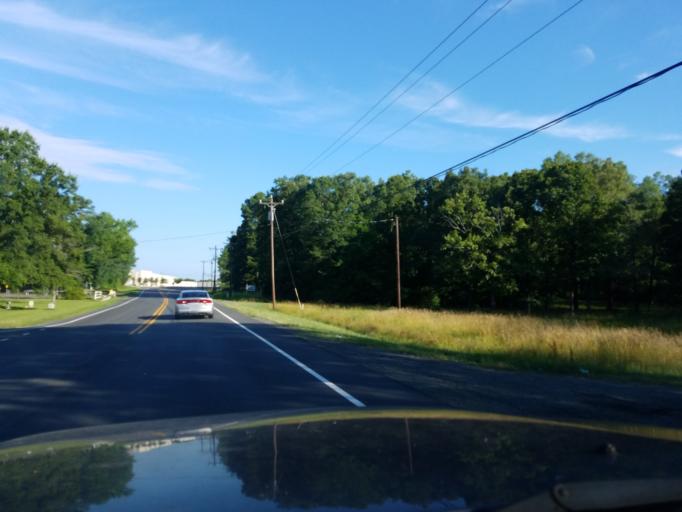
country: US
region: North Carolina
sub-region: Granville County
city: Butner
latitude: 36.1223
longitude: -78.7482
